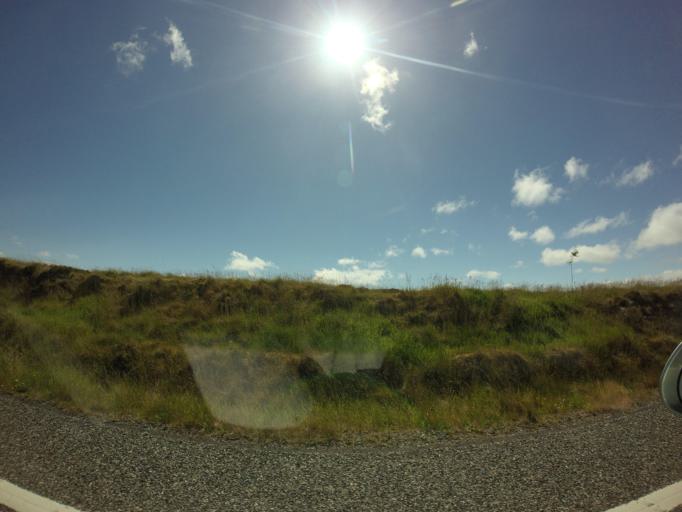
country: GB
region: Scotland
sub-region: Eilean Siar
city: Harris
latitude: 58.1937
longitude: -6.7150
